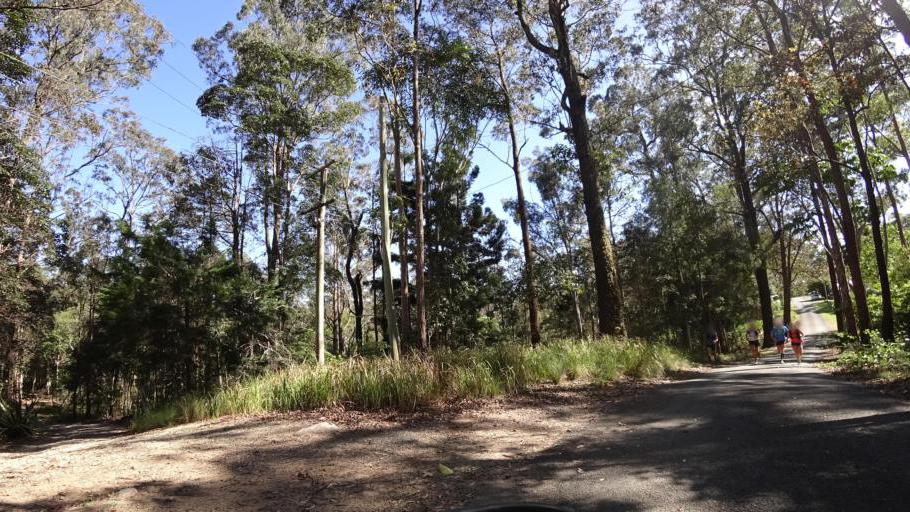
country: AU
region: Queensland
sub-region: Moreton Bay
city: Highvale
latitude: -27.3997
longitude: 152.7825
